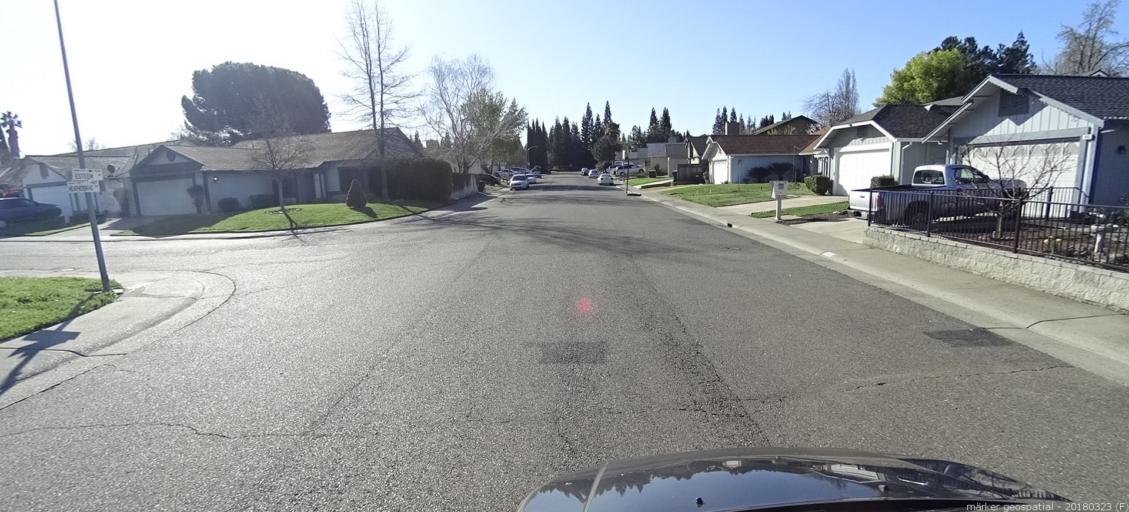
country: US
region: California
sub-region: Sacramento County
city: Foothill Farms
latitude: 38.7019
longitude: -121.3534
